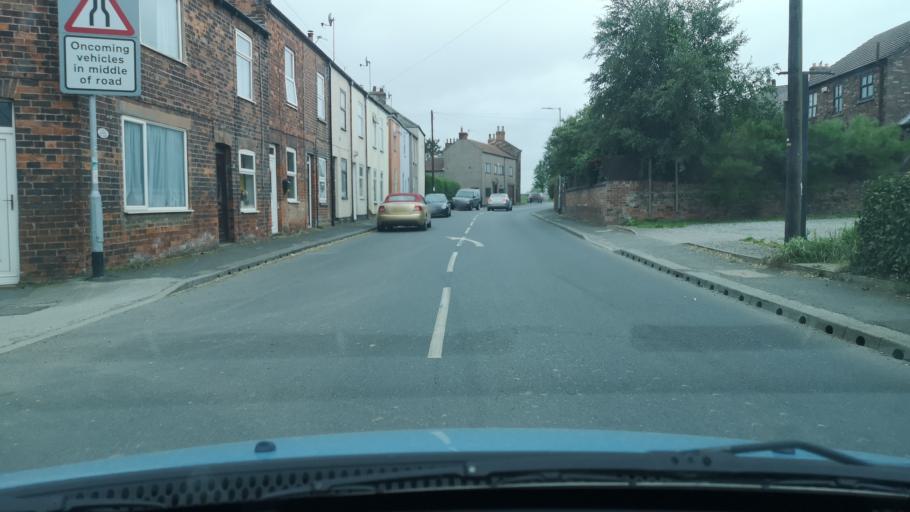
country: GB
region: England
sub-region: East Riding of Yorkshire
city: Skelton
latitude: 53.6894
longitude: -0.8382
